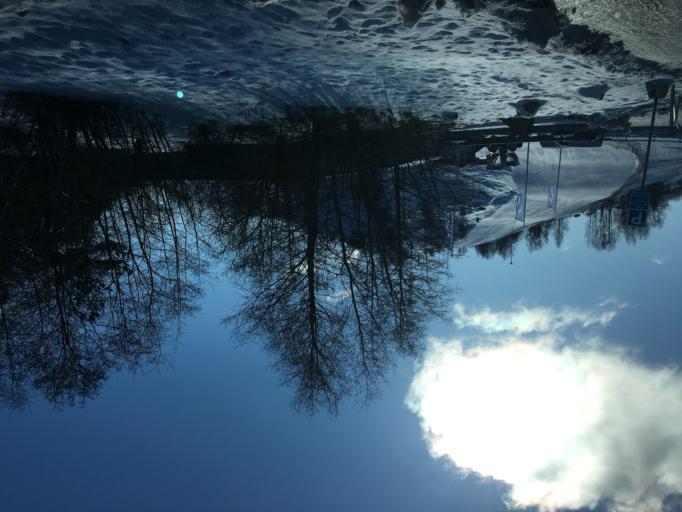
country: SE
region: Vaestmanland
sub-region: Vasteras
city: Vasteras
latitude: 59.6265
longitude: 16.4833
